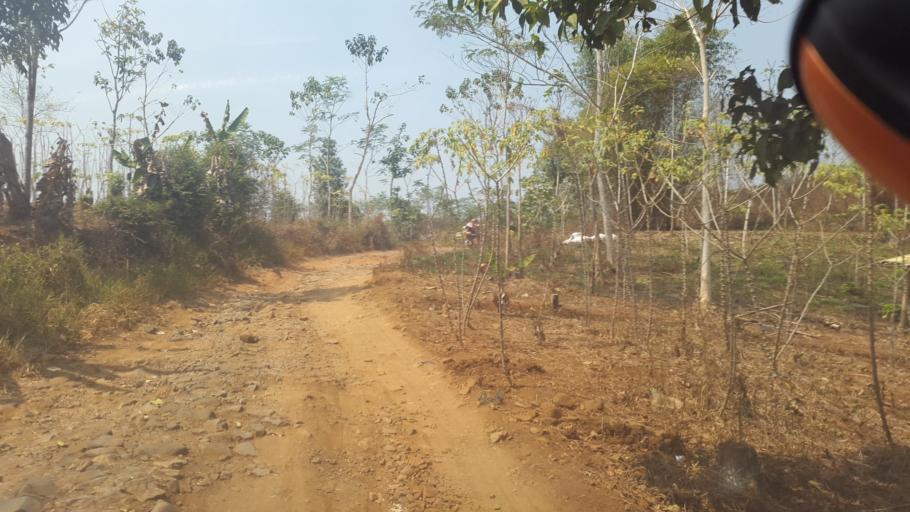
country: ID
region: West Java
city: Ciroyom
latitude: -7.0984
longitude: 106.8284
